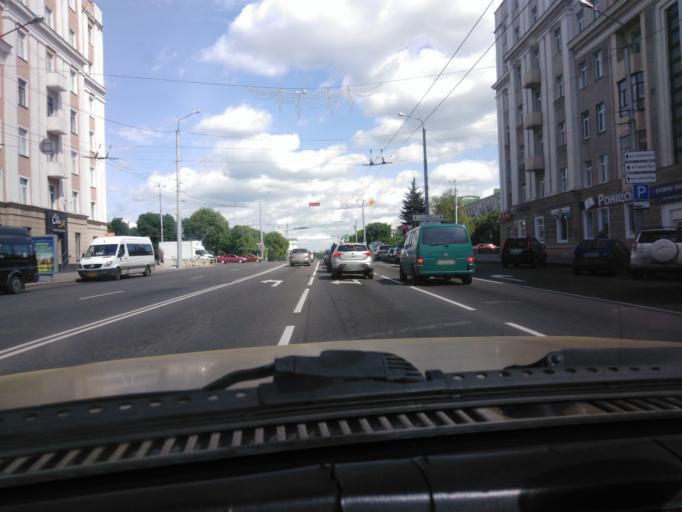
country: BY
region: Mogilev
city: Mahilyow
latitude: 53.9089
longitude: 30.3394
